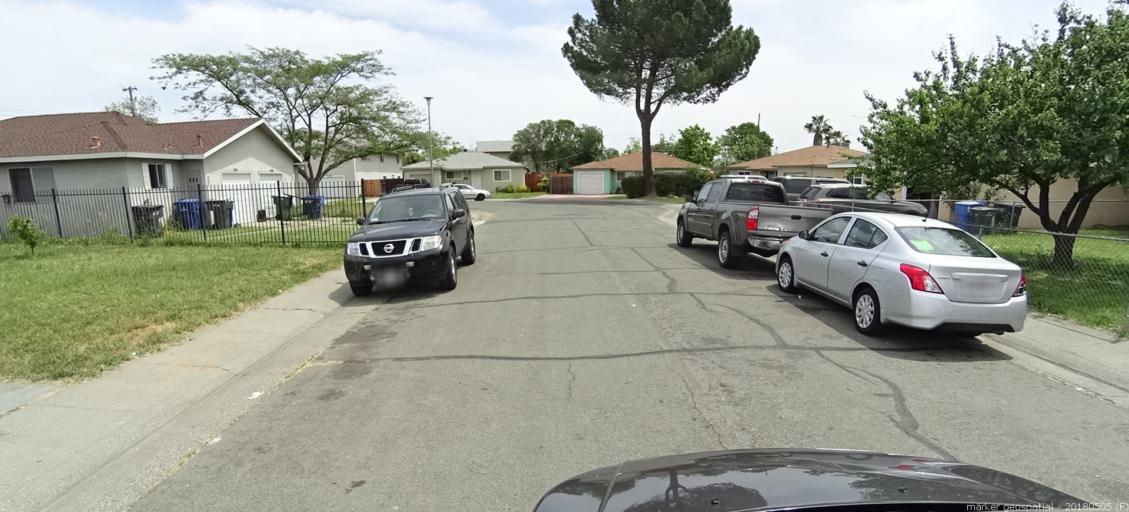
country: US
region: California
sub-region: Sacramento County
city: Rio Linda
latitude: 38.6419
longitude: -121.4347
